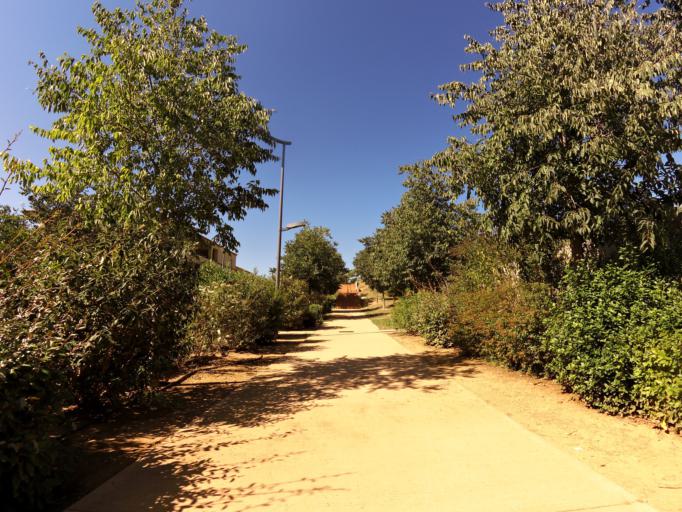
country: FR
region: Languedoc-Roussillon
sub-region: Departement du Gard
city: Vergeze
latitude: 43.7399
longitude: 4.2262
